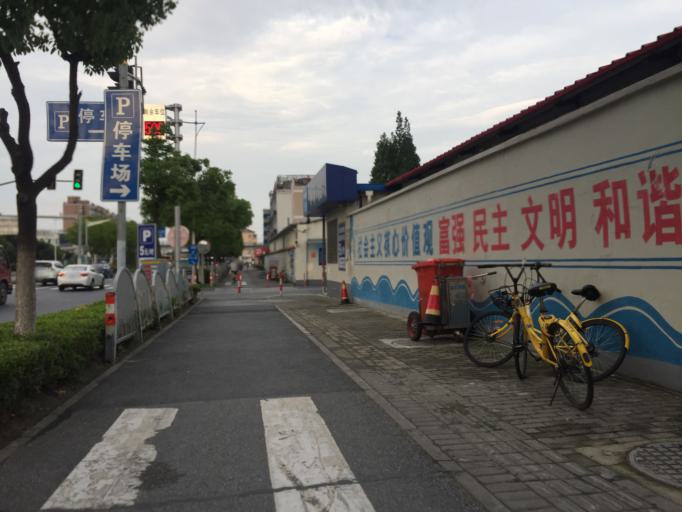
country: CN
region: Shanghai Shi
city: Huamu
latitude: 31.1903
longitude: 121.5459
